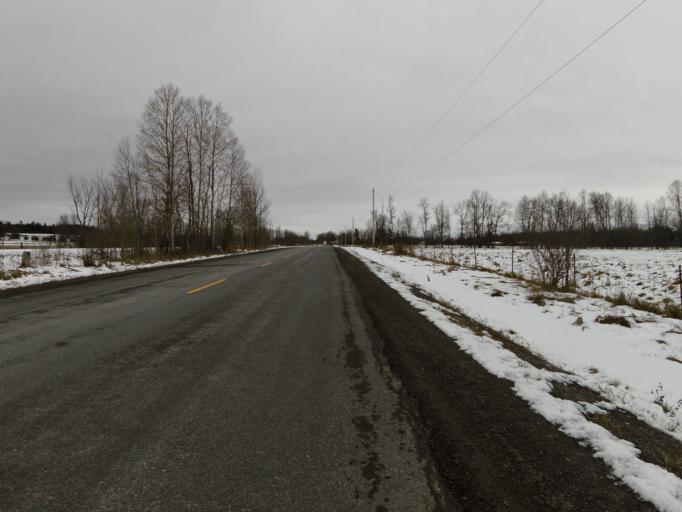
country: CA
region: Ontario
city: Carleton Place
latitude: 45.2736
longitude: -76.2390
